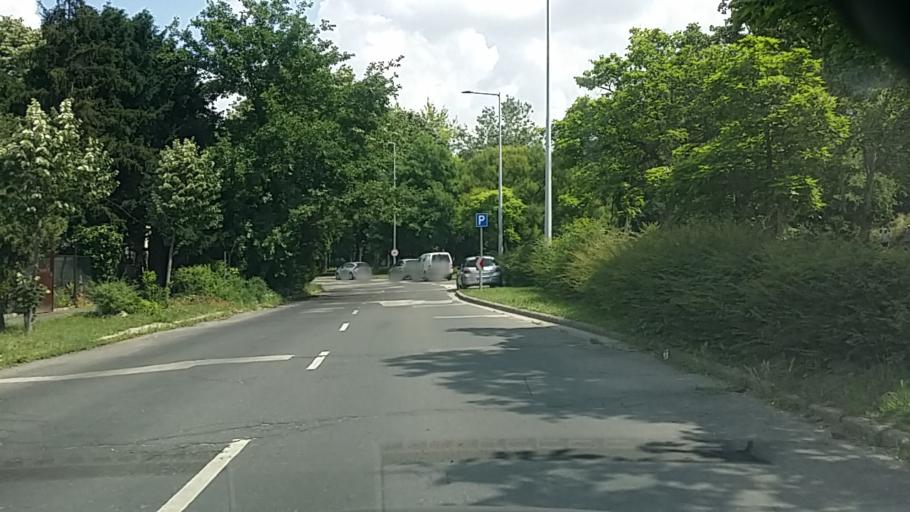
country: HU
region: Budapest
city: Budapest XV. keruelet
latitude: 47.5404
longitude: 19.1367
